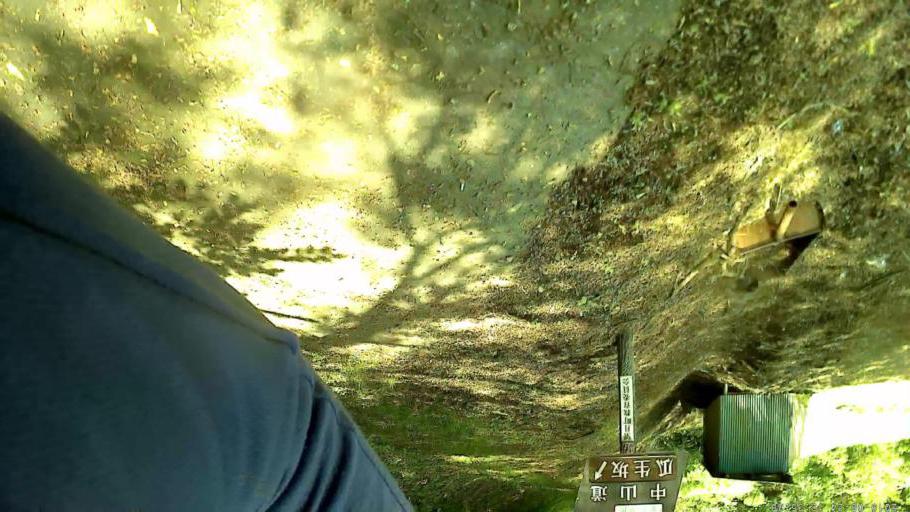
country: JP
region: Nagano
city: Komoro
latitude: 36.2655
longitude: 138.3677
